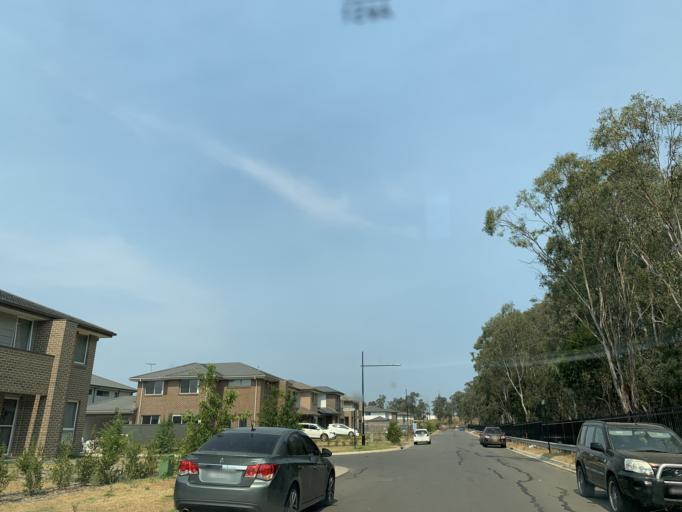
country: AU
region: New South Wales
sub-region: Blacktown
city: Blackett
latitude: -33.7134
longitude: 150.8179
